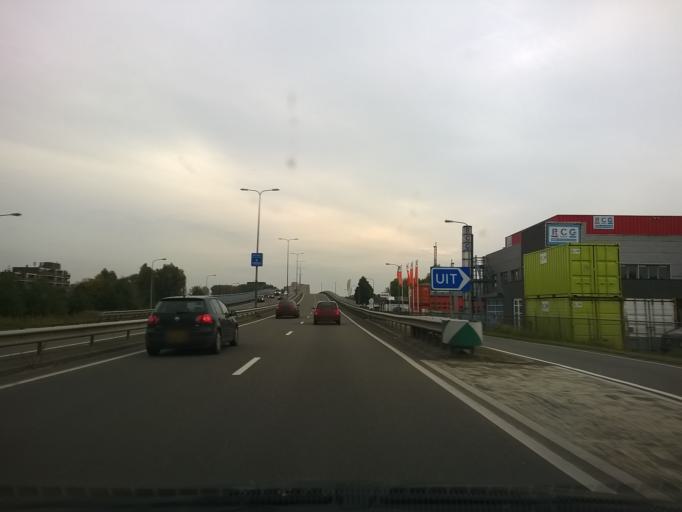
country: NL
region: Groningen
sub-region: Gemeente Groningen
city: Groningen
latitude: 53.2153
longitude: 6.5402
